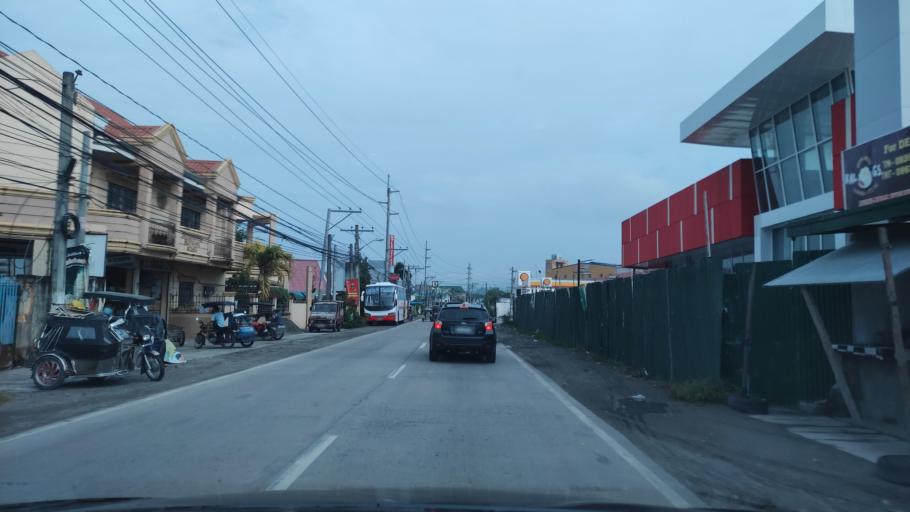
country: PH
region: Central Luzon
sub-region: Province of Pampanga
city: Arayat
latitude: 15.1453
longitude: 120.7688
